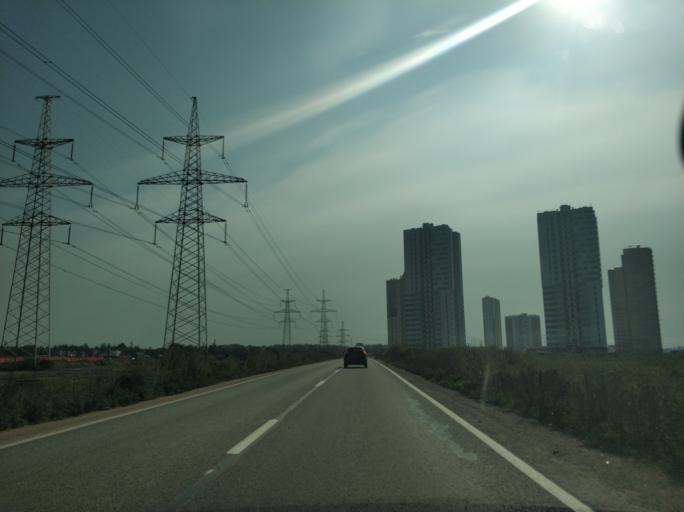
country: RU
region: St.-Petersburg
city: Krasnogvargeisky
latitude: 60.0142
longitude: 30.4782
